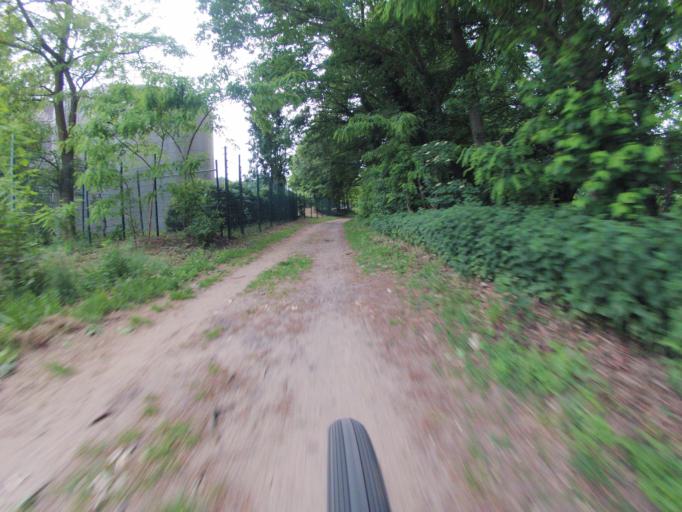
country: DE
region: North Rhine-Westphalia
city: Emsdetten
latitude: 52.1701
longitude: 7.5673
